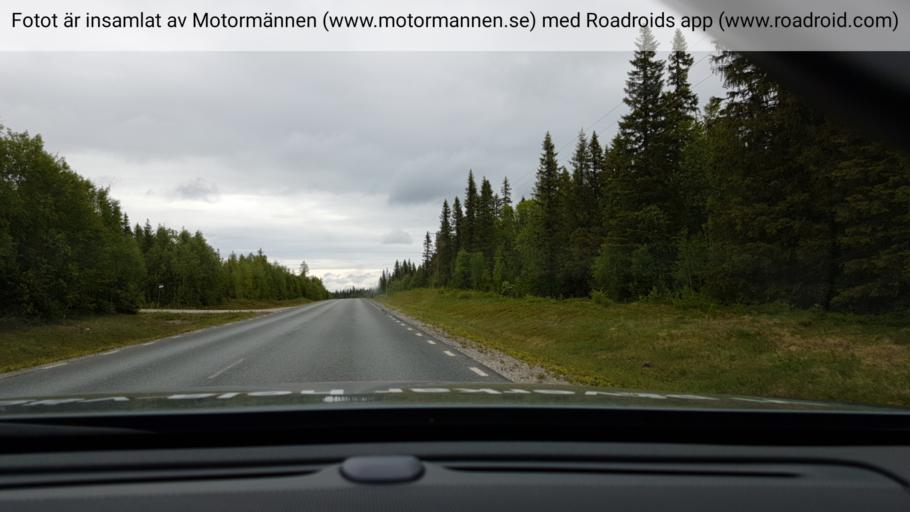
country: SE
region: Vaesterbotten
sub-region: Lycksele Kommun
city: Soderfors
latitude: 64.4384
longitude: 18.1102
